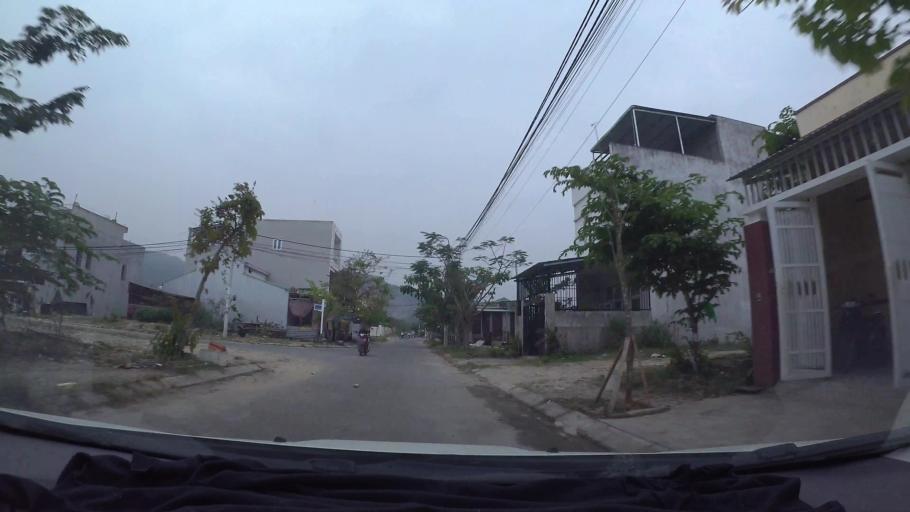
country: VN
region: Da Nang
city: Thanh Khe
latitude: 16.0434
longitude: 108.1772
